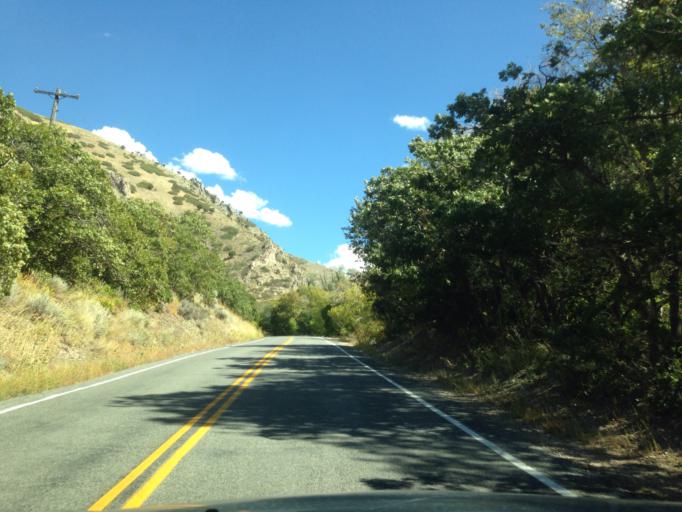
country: US
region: Utah
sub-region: Salt Lake County
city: Mount Olympus
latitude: 40.6896
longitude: -111.7811
